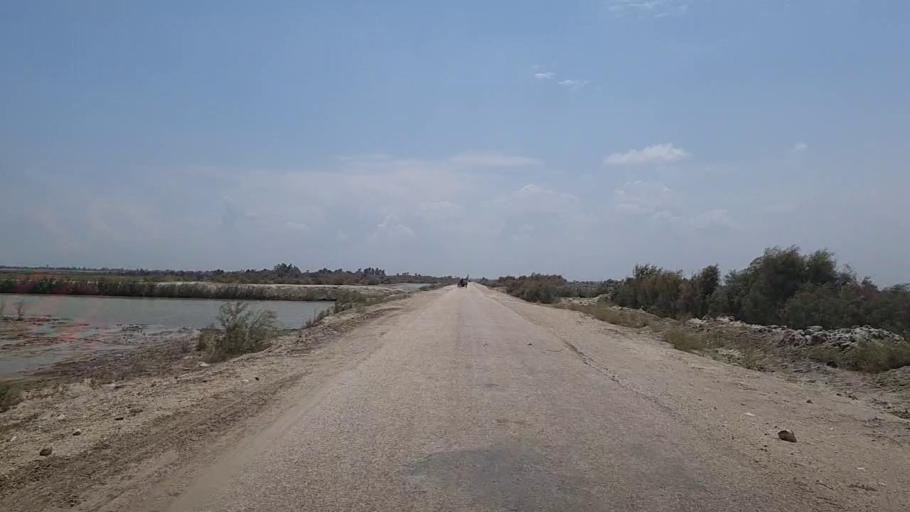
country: PK
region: Sindh
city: Kandhkot
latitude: 28.2862
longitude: 69.1658
